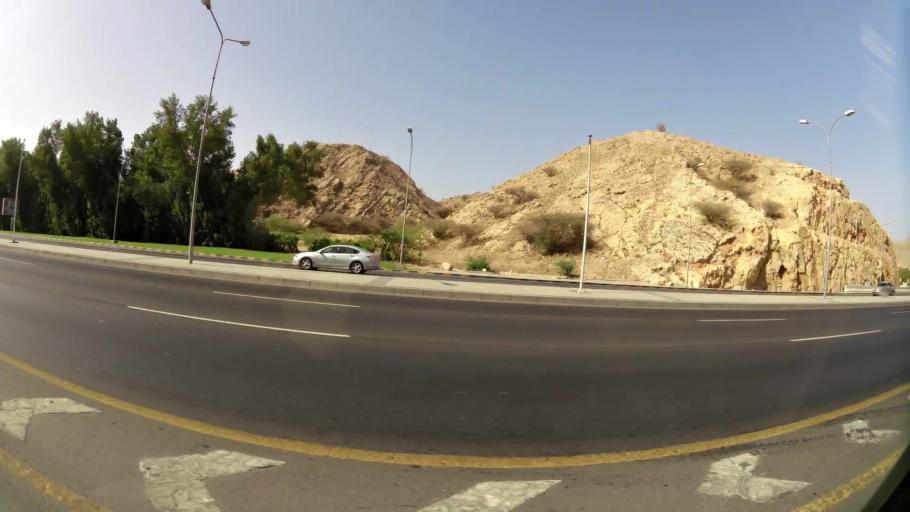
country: OM
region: Muhafazat Masqat
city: Muscat
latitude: 23.6072
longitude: 58.5028
